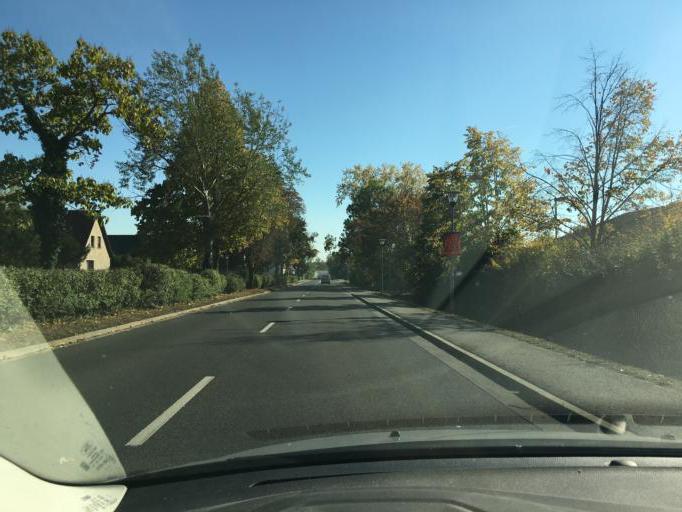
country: DE
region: Saxony-Anhalt
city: Wanzleben
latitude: 52.0587
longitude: 11.4462
